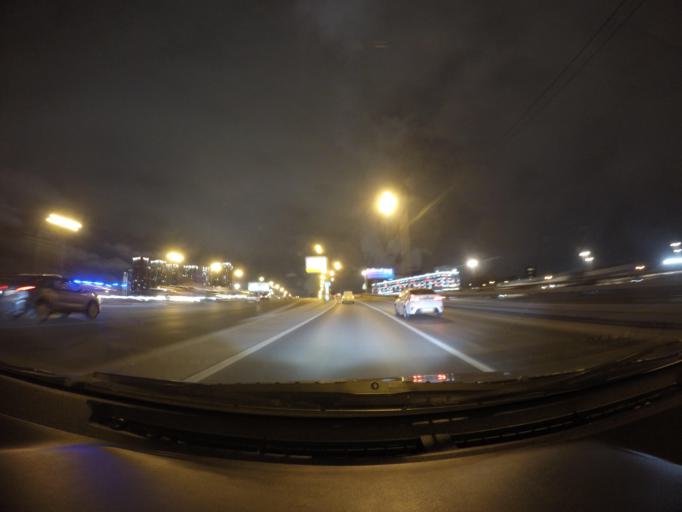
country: RU
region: Moscow
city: Taganskiy
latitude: 55.7190
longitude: 37.7045
